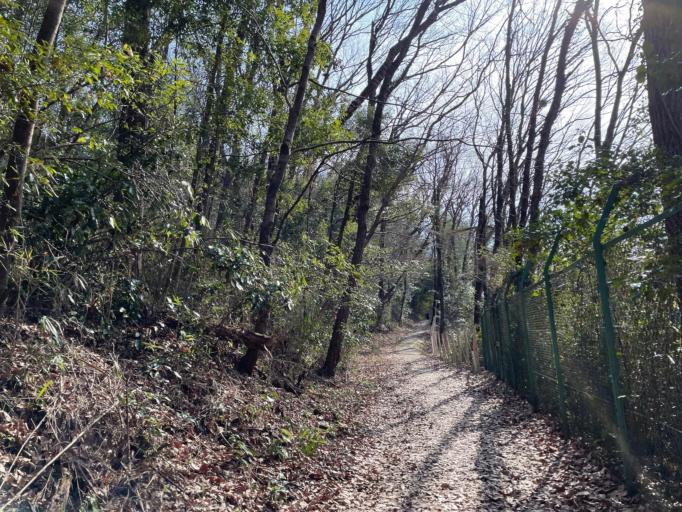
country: JP
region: Tokyo
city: Higashimurayama-shi
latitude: 35.7608
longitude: 139.3969
